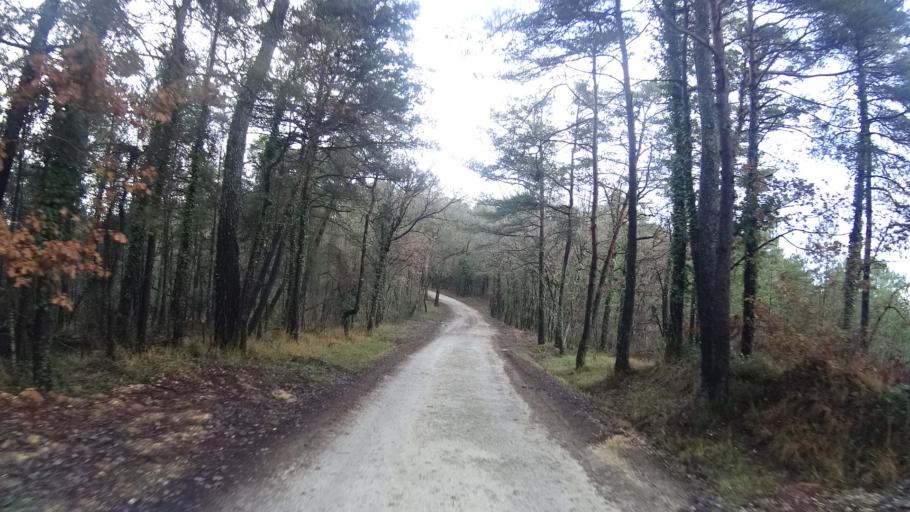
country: FR
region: Aquitaine
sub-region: Departement de la Dordogne
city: Antonne-et-Trigonant
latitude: 45.2107
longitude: 0.8687
